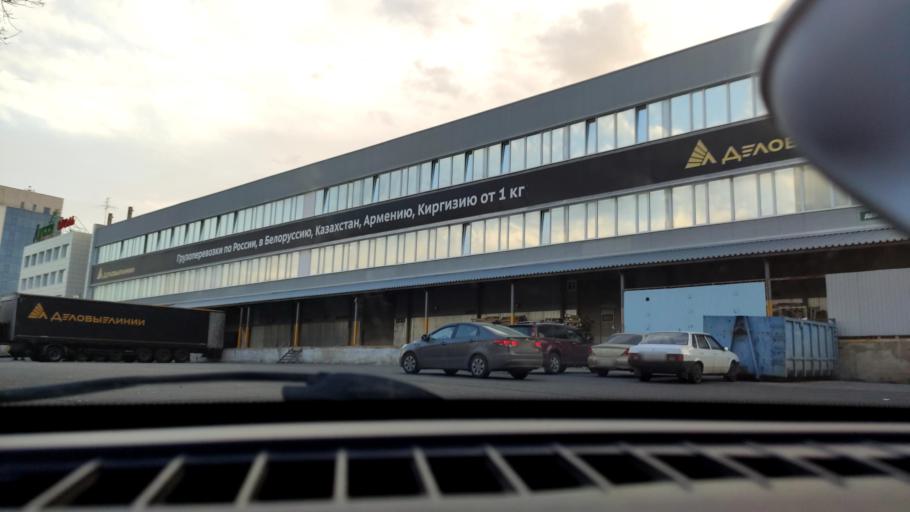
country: RU
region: Samara
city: Samara
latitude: 53.2736
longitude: 50.2259
